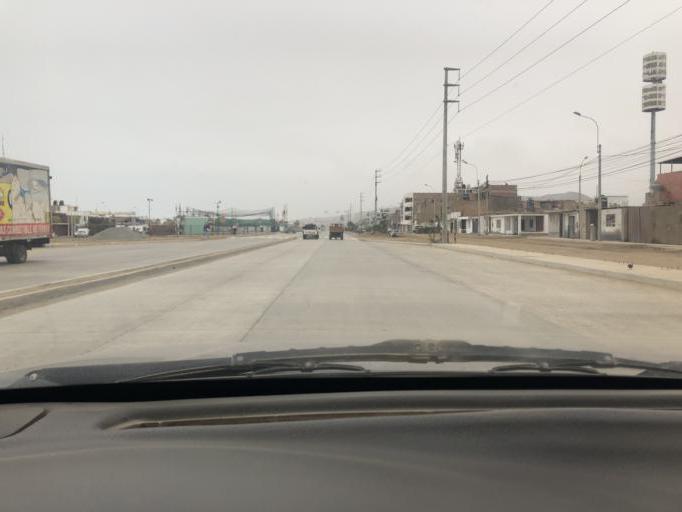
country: PE
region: Lima
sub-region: Lima
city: San Bartolo
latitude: -12.3674
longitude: -76.7924
